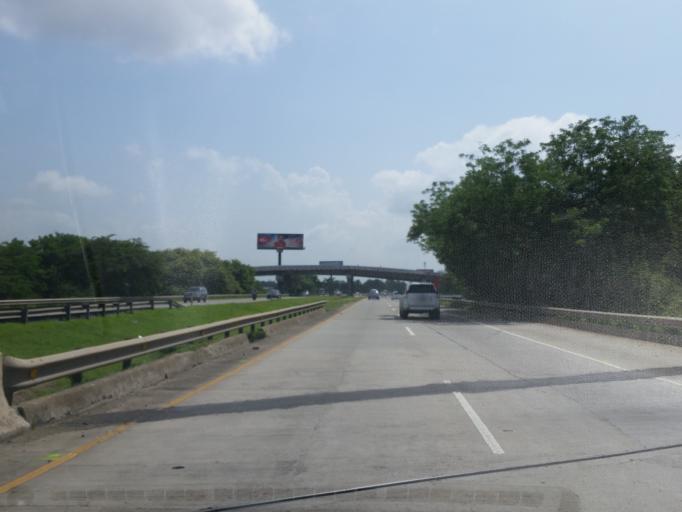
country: PA
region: Panama
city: San Miguelito
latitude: 9.0324
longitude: -79.4437
